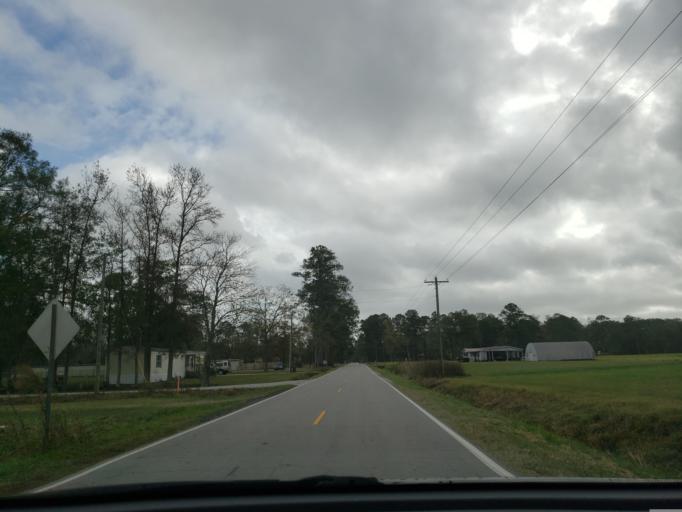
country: US
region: North Carolina
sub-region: Onslow County
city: Jacksonville
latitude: 34.7321
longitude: -77.5831
